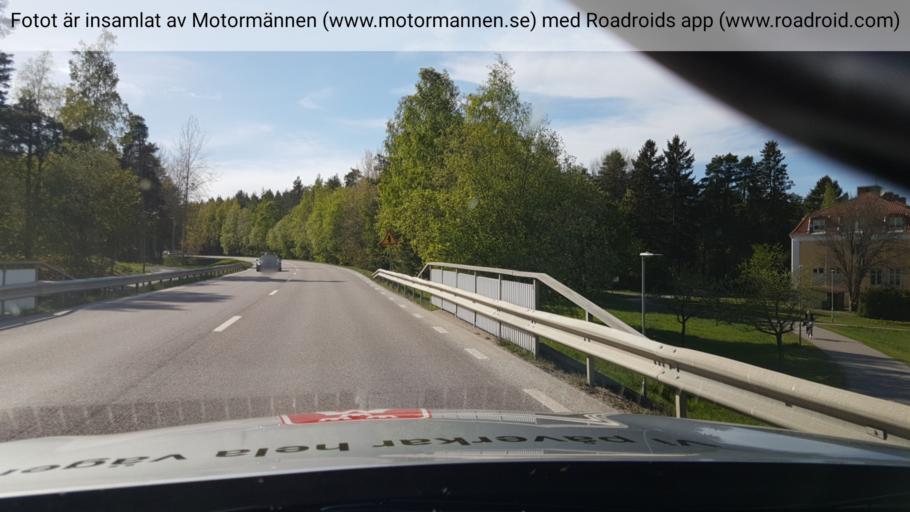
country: SE
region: Vaestmanland
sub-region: Sala Kommun
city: Sala
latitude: 59.9100
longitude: 16.6075
